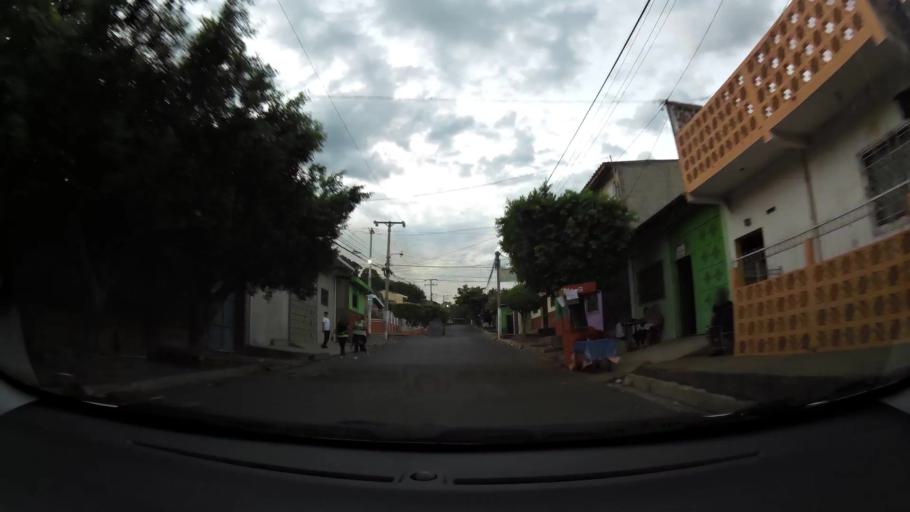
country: SV
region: San Vicente
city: San Vicente
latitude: 13.6418
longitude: -88.7911
